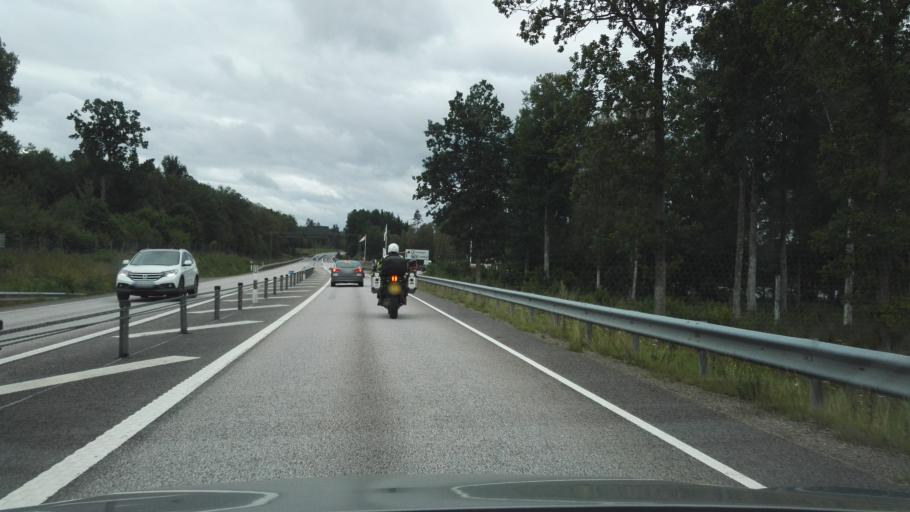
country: SE
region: Kronoberg
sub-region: Vaxjo Kommun
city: Rottne
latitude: 56.9797
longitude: 14.9827
